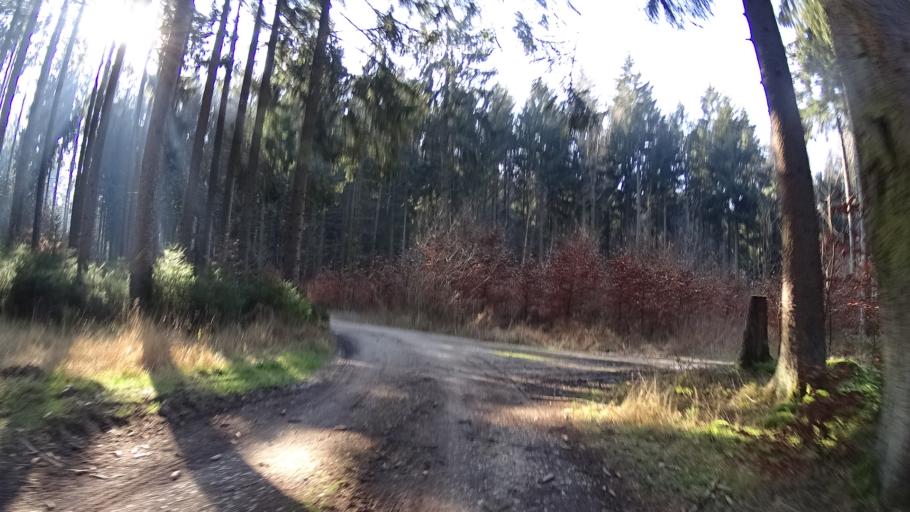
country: DE
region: Bavaria
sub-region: Upper Bavaria
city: Stammham
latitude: 48.8660
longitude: 11.4272
